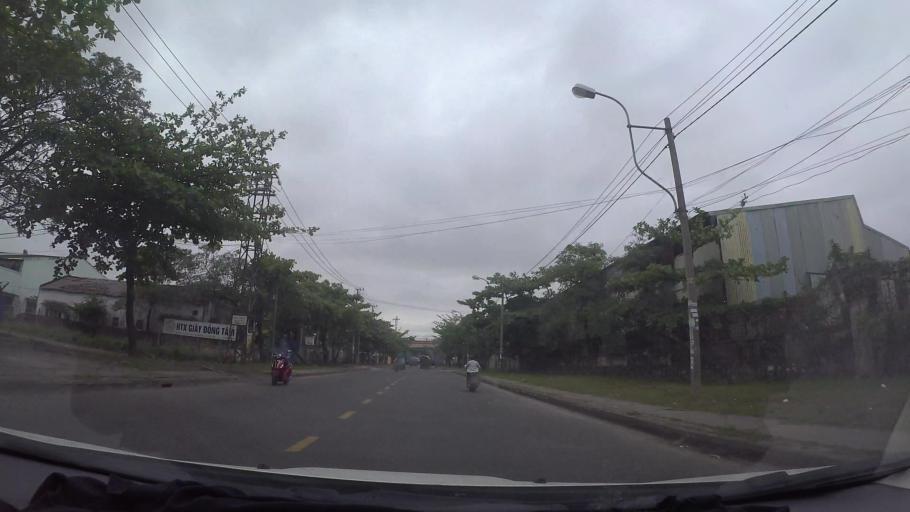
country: VN
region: Da Nang
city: Lien Chieu
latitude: 16.0830
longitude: 108.1402
